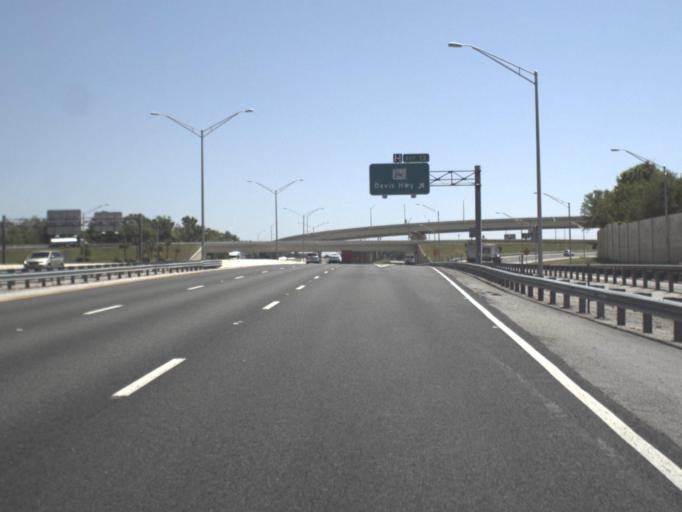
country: US
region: Florida
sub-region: Escambia County
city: Ferry Pass
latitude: 30.5034
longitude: -87.2342
